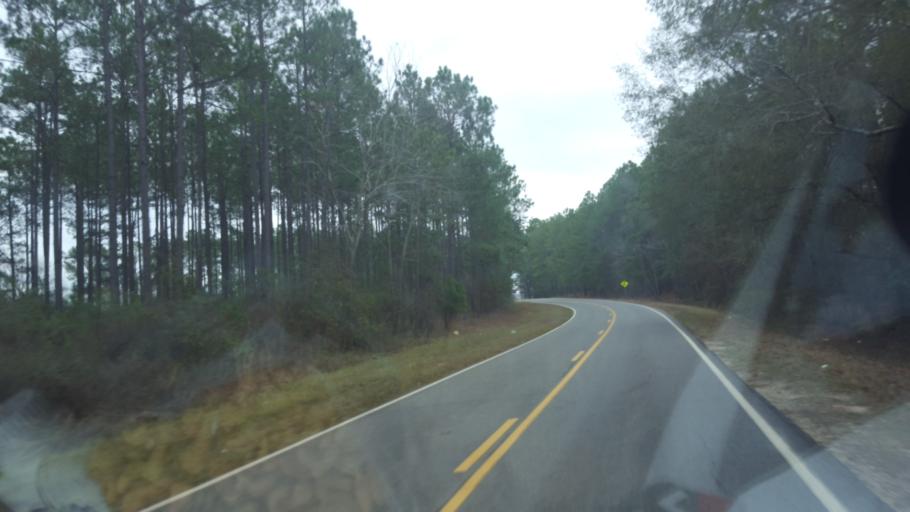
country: US
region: Georgia
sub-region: Wilcox County
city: Rochelle
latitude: 31.7857
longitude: -83.4342
